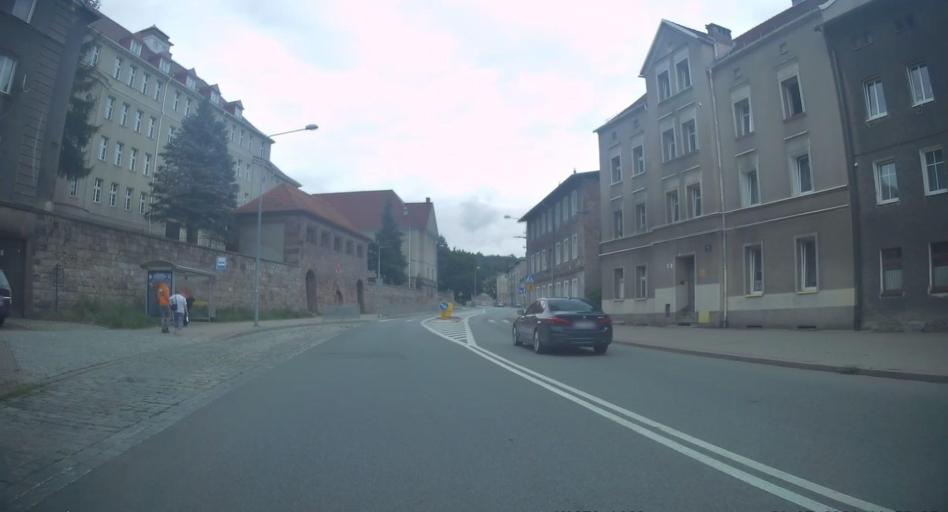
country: PL
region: Lower Silesian Voivodeship
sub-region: Powiat walbrzyski
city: Walbrzych
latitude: 50.7788
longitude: 16.2962
